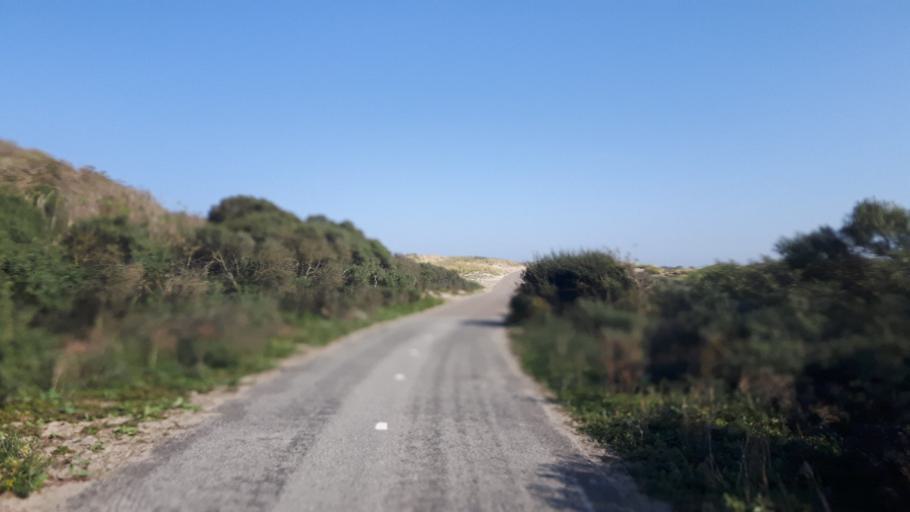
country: NL
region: North Holland
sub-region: Gemeente Zandvoort
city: Zandvoort
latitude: 52.3530
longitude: 4.5131
